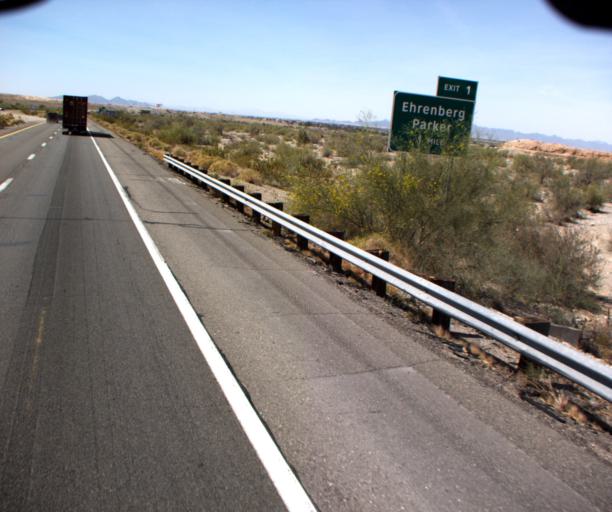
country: US
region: Arizona
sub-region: La Paz County
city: Ehrenberg
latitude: 33.6053
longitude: -114.5007
